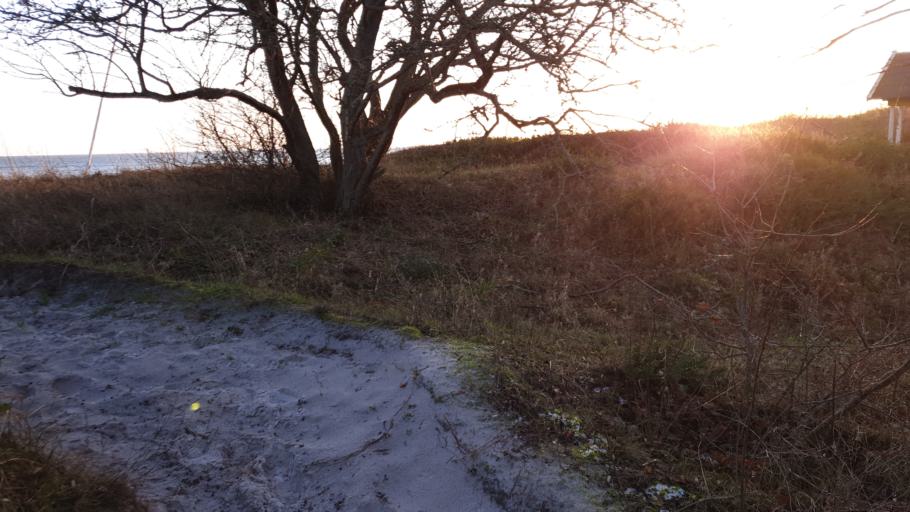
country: SE
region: Skane
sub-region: Vellinge Kommun
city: Skanor med Falsterbo
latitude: 55.3853
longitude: 12.8299
